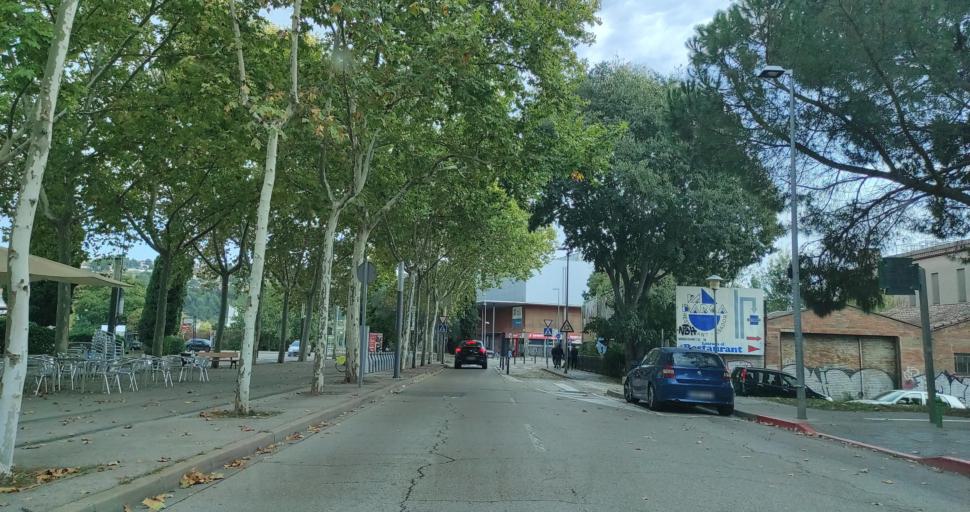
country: ES
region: Catalonia
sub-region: Provincia de Girona
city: Girona
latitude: 41.9921
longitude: 2.8173
